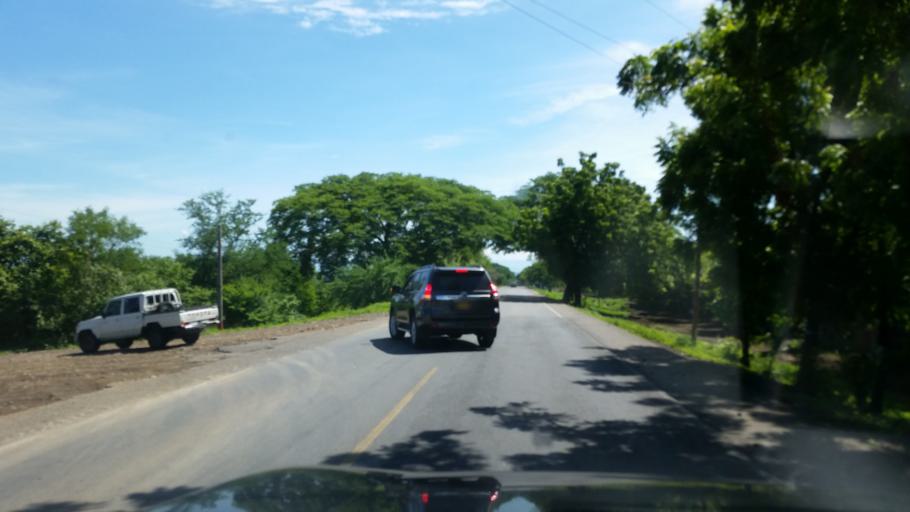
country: NI
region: Chinandega
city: Puerto Morazan
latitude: 12.7667
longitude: -87.0586
